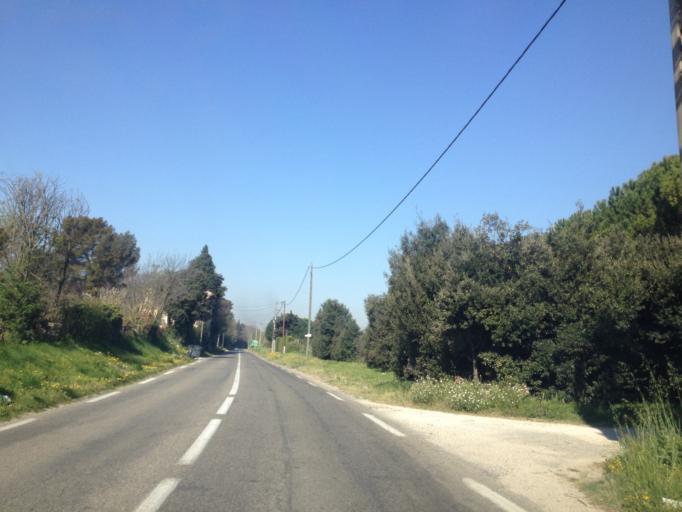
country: FR
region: Provence-Alpes-Cote d'Azur
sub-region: Departement du Vaucluse
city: Loriol-du-Comtat
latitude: 44.0685
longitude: 5.0237
